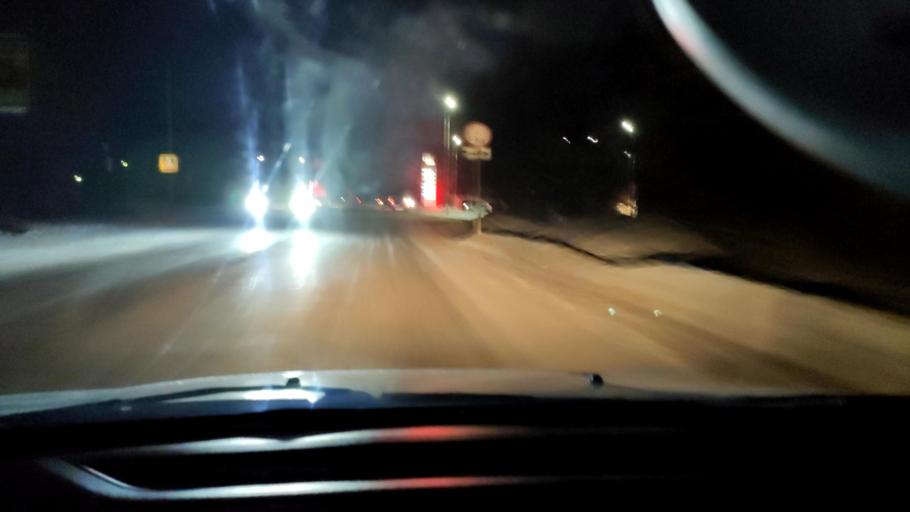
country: RU
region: Perm
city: Overyata
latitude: 58.0047
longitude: 55.9116
